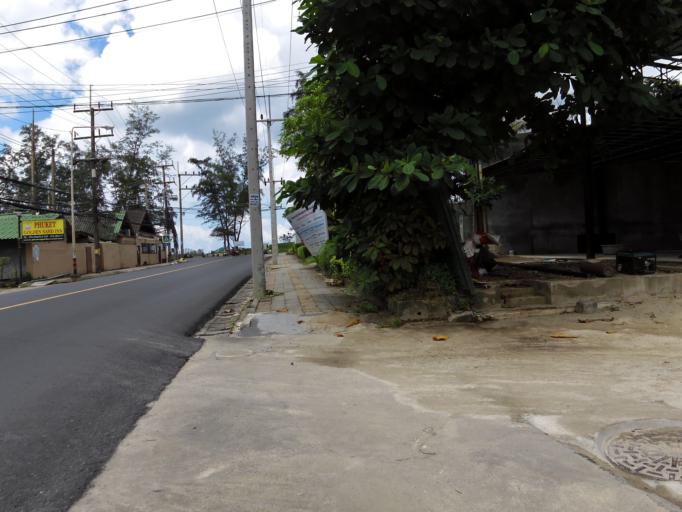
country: TH
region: Phuket
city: Ban Karon
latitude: 7.8506
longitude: 98.2934
